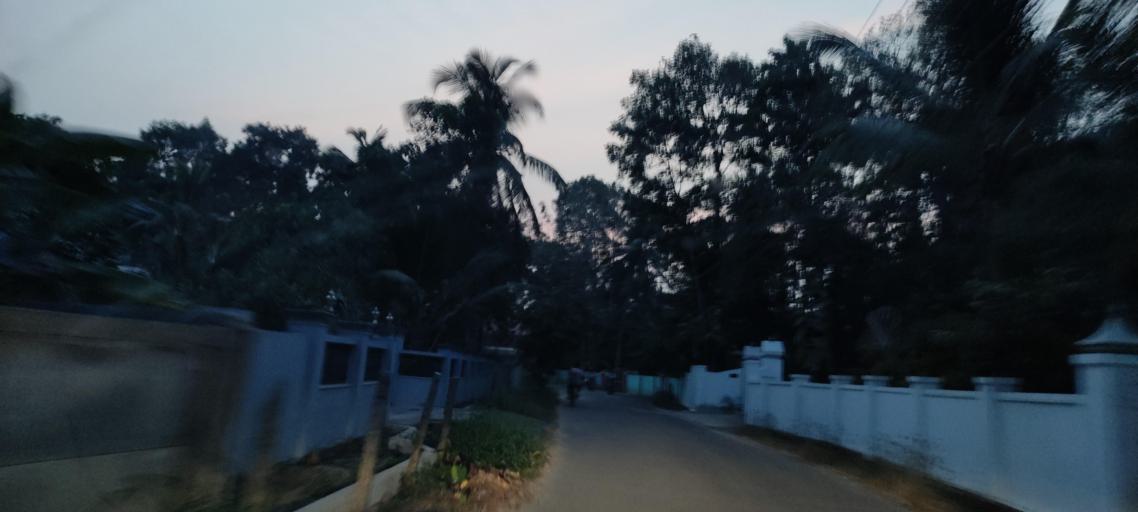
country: IN
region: Kerala
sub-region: Alappuzha
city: Mavelikara
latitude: 9.3216
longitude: 76.4596
